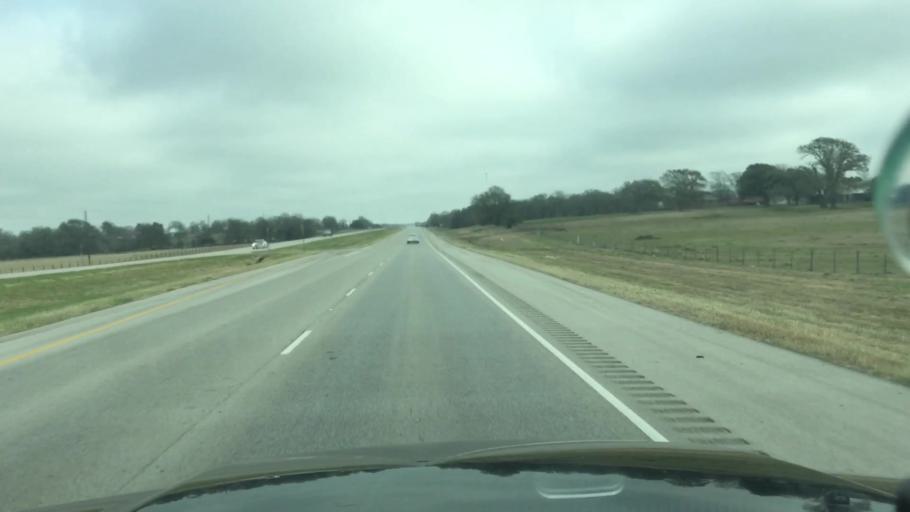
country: US
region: Texas
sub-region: Lee County
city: Giddings
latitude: 30.1454
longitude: -96.7204
